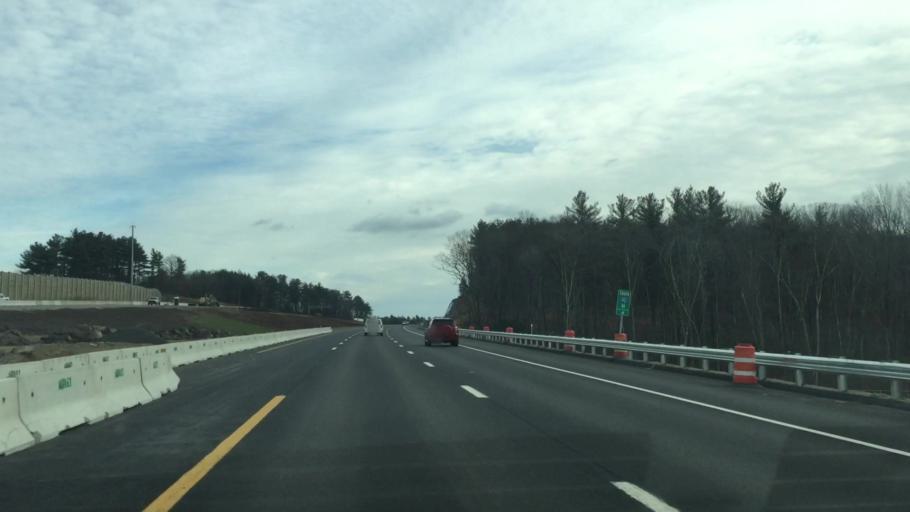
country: US
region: New Hampshire
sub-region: Rockingham County
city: Derry
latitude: 42.8587
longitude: -71.3278
